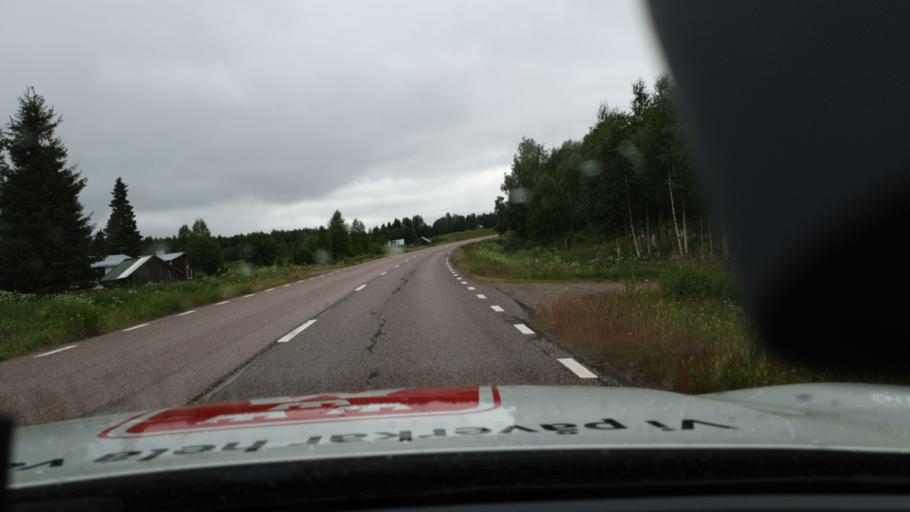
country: FI
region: Lapland
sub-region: Torniolaakso
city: Pello
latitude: 66.9616
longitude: 23.8236
